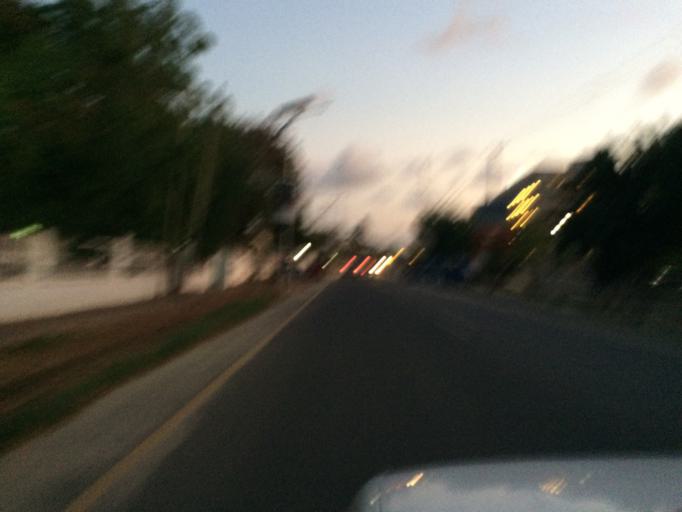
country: TZ
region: Dar es Salaam
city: Magomeni
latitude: -6.7530
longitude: 39.2734
